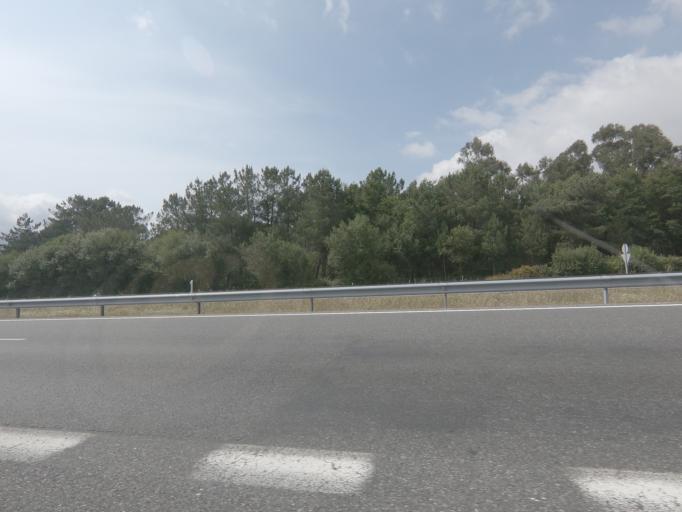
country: ES
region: Galicia
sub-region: Provincia de Pontevedra
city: Covelo
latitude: 42.2035
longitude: -8.2741
